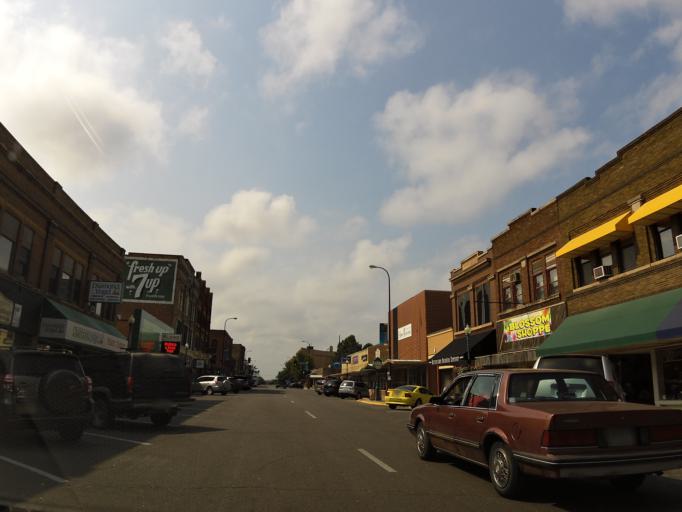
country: US
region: South Dakota
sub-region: Codington County
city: Watertown
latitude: 44.8998
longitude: -97.1116
